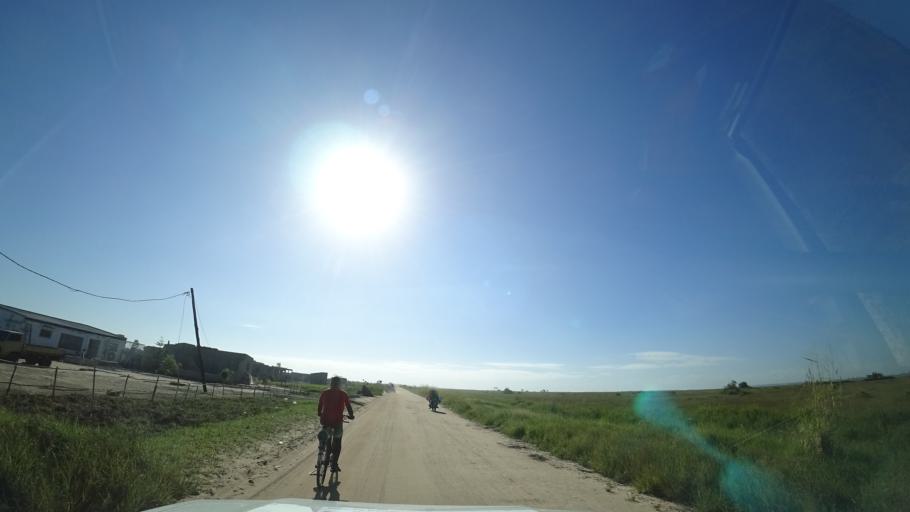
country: MZ
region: Sofala
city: Beira
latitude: -19.7621
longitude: 34.9086
